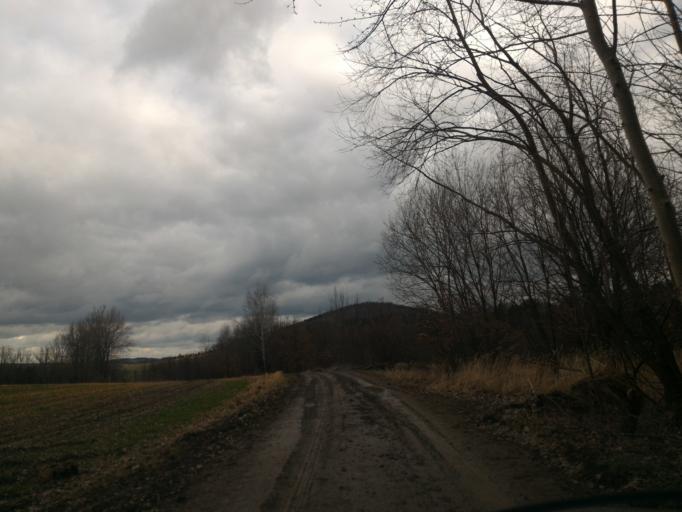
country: DE
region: Saxony
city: Grossschonau
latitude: 50.8803
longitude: 14.6863
